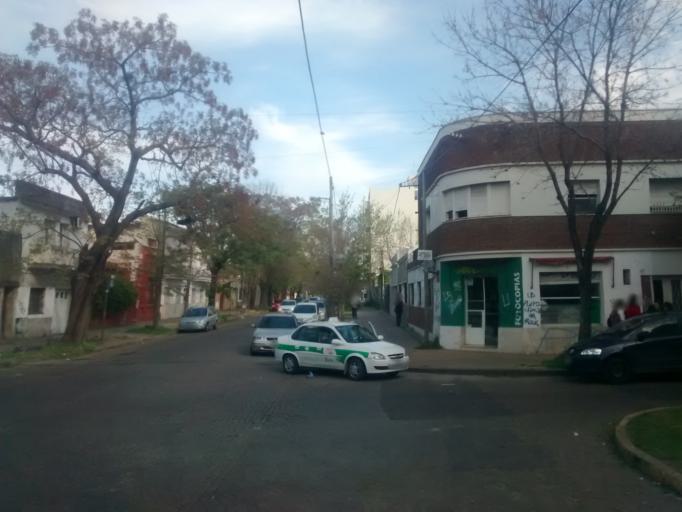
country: AR
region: Buenos Aires
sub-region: Partido de La Plata
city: La Plata
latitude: -34.9297
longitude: -57.9389
